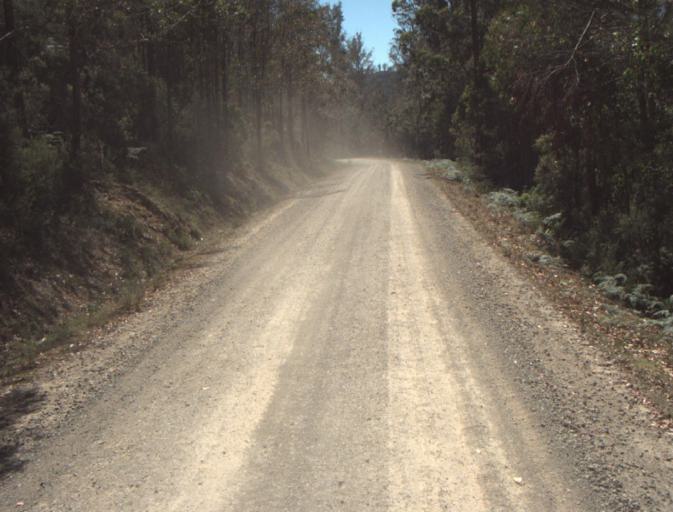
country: AU
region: Tasmania
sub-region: Dorset
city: Scottsdale
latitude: -41.3910
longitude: 147.5100
